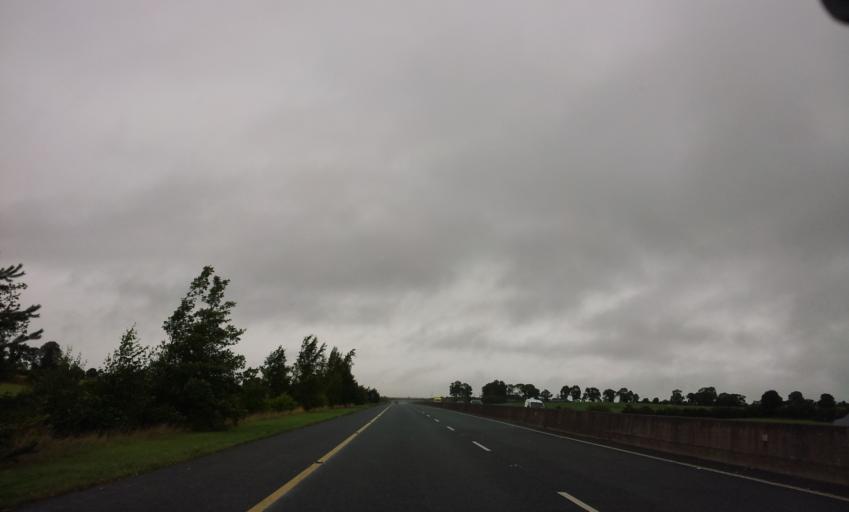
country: IE
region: Munster
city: Cahir
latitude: 52.4425
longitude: -7.9106
